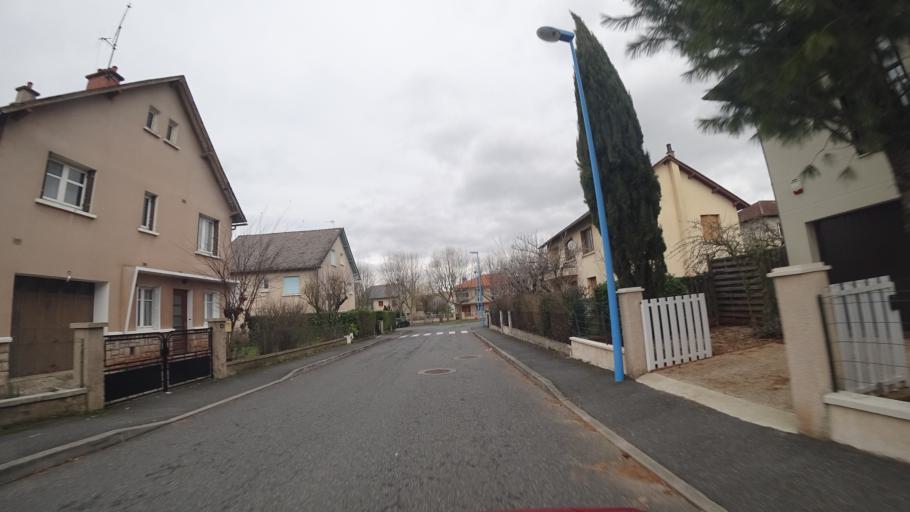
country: FR
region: Midi-Pyrenees
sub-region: Departement de l'Aveyron
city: Rodez
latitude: 44.3684
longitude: 2.5930
